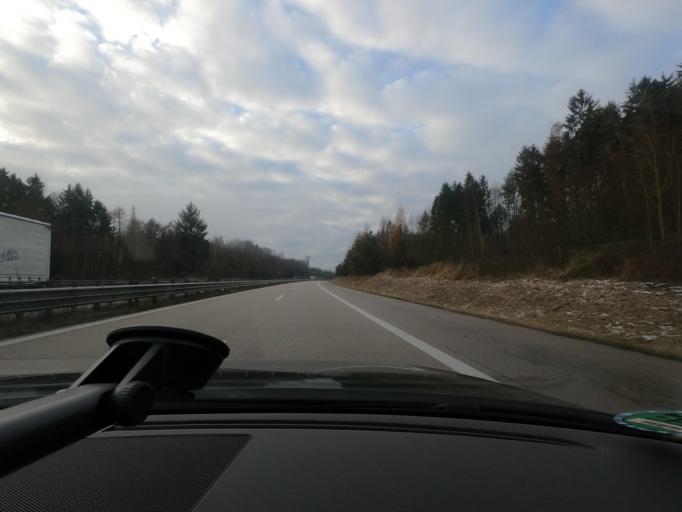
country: DE
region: Bavaria
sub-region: Upper Franconia
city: Lichtenfels
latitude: 50.2039
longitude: 11.0431
